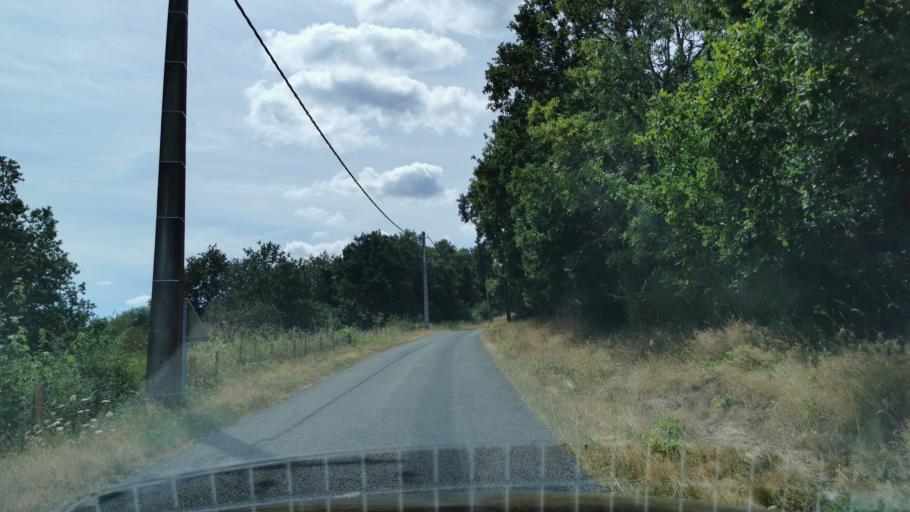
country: FR
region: Bourgogne
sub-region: Departement de Saone-et-Loire
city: Marmagne
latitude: 46.8091
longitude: 4.3088
